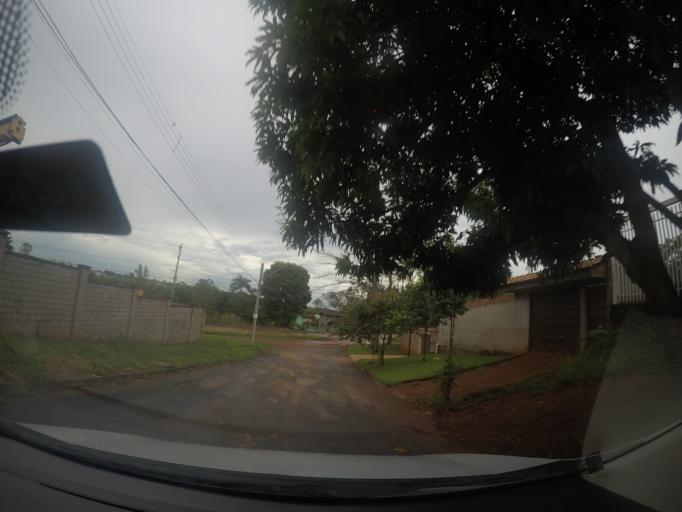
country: BR
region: Goias
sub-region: Goiania
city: Goiania
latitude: -16.6286
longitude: -49.2368
